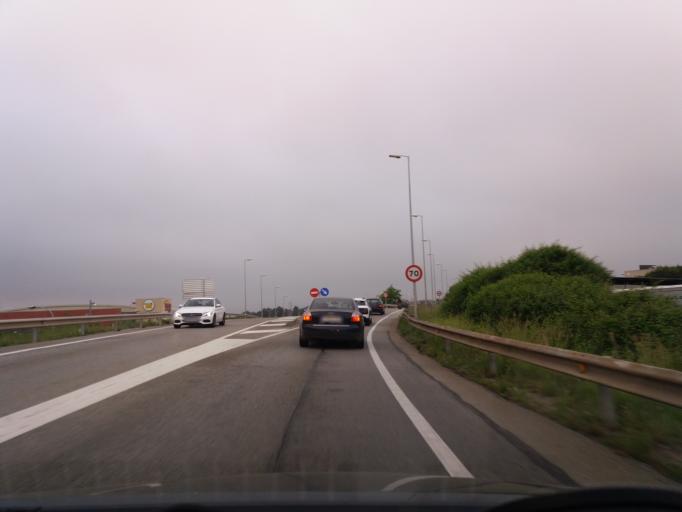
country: ES
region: Catalonia
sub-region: Provincia de Barcelona
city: Abrera
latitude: 41.5189
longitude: 1.8981
